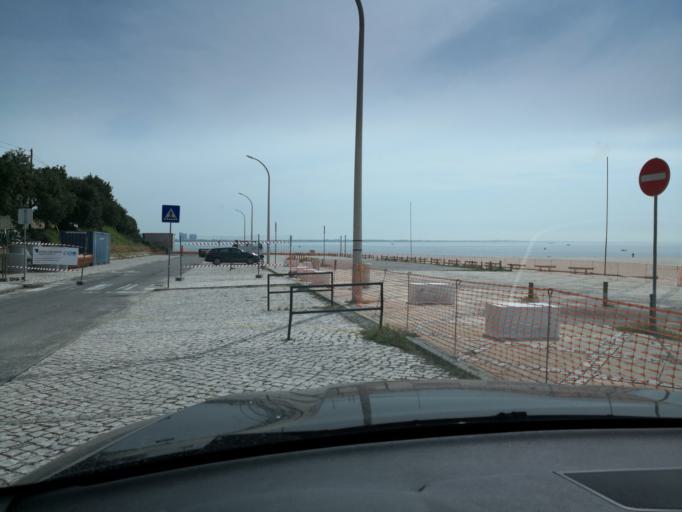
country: PT
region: Setubal
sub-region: Setubal
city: Setubal
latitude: 38.4849
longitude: -8.9441
